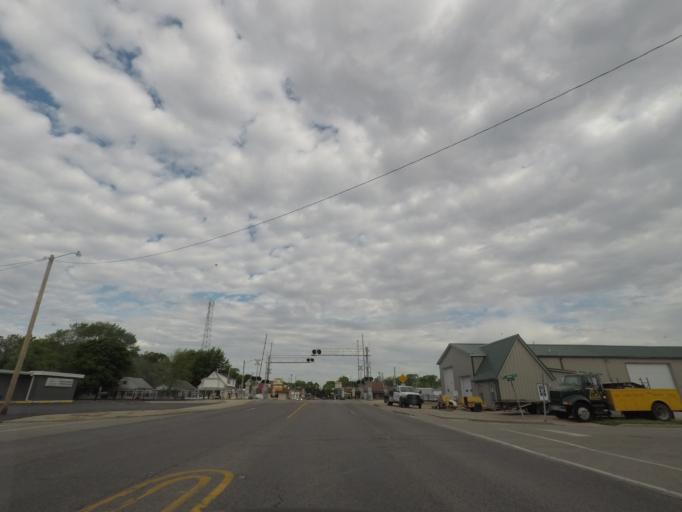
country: US
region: Illinois
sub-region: Logan County
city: Lincoln
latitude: 40.1521
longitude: -89.3580
